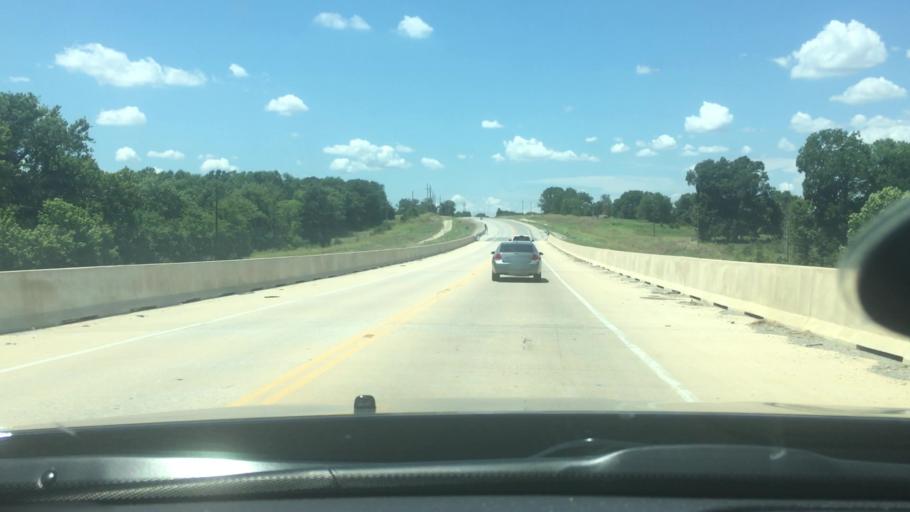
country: US
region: Oklahoma
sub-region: Bryan County
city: Durant
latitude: 33.9978
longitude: -96.2400
